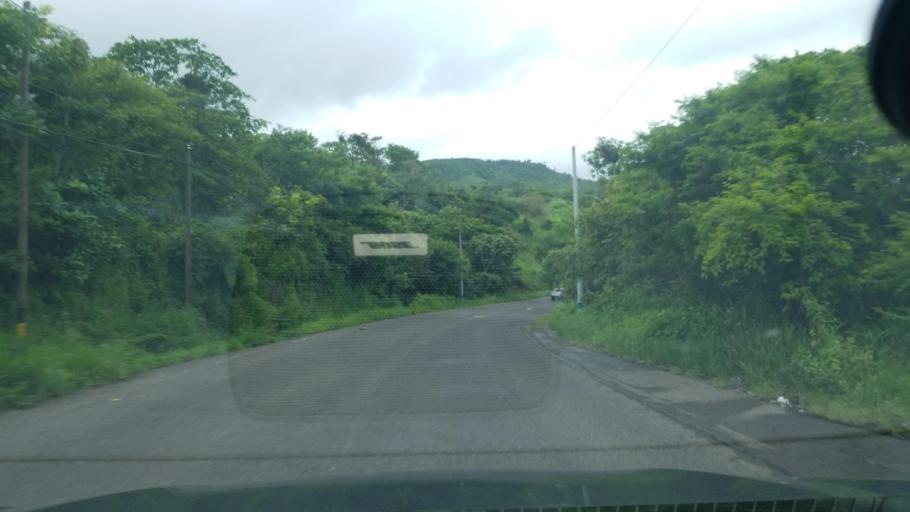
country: HN
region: Choluteca
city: San Marcos de Colon
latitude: 13.4197
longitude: -86.8342
